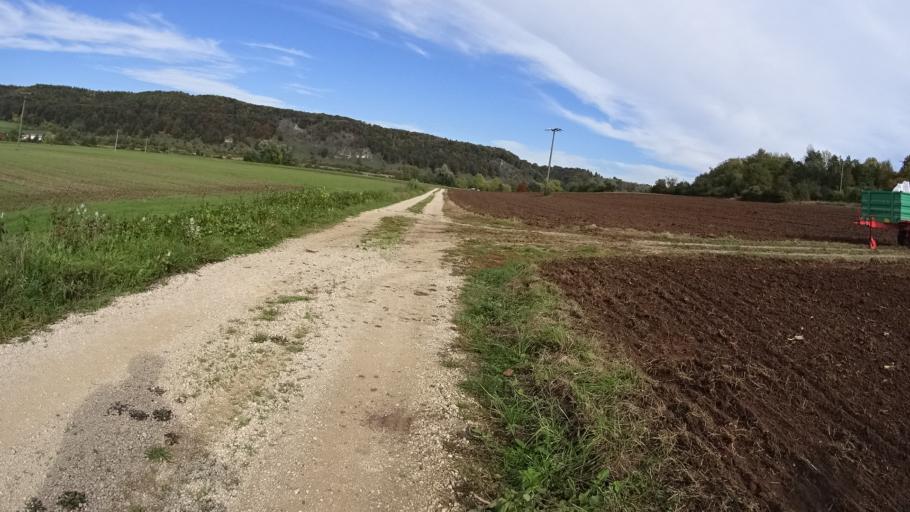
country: DE
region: Bavaria
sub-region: Upper Bavaria
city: Walting
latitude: 48.9320
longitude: 11.3160
